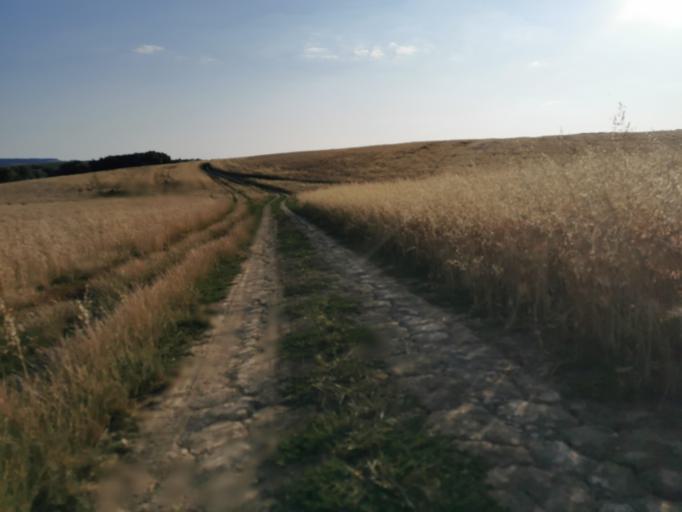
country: SK
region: Trnavsky
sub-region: Okres Skalica
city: Skalica
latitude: 48.7914
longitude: 17.2859
